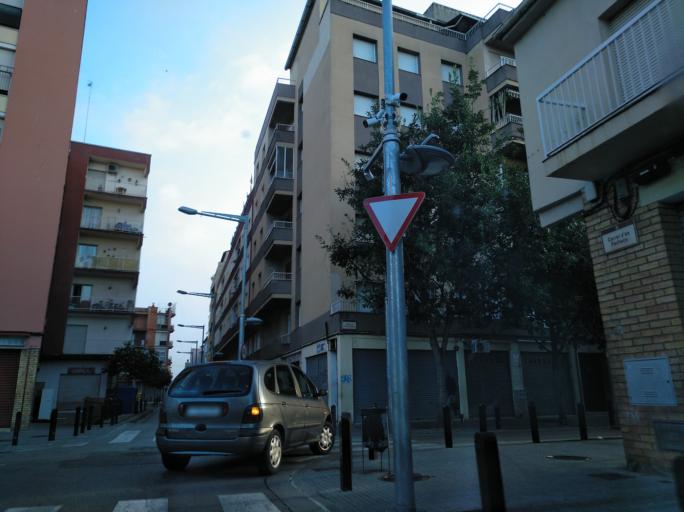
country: ES
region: Catalonia
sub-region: Provincia de Girona
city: Salt
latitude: 41.9728
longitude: 2.7883
